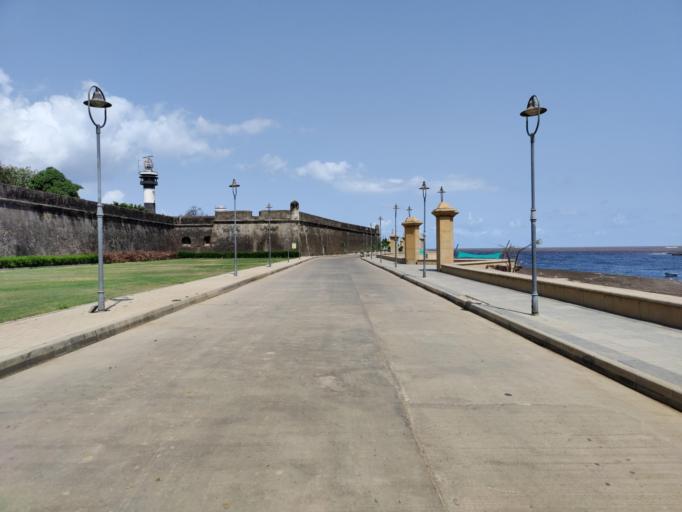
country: IN
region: Daman and Diu
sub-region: Daman District
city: Daman
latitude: 20.4102
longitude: 72.8327
